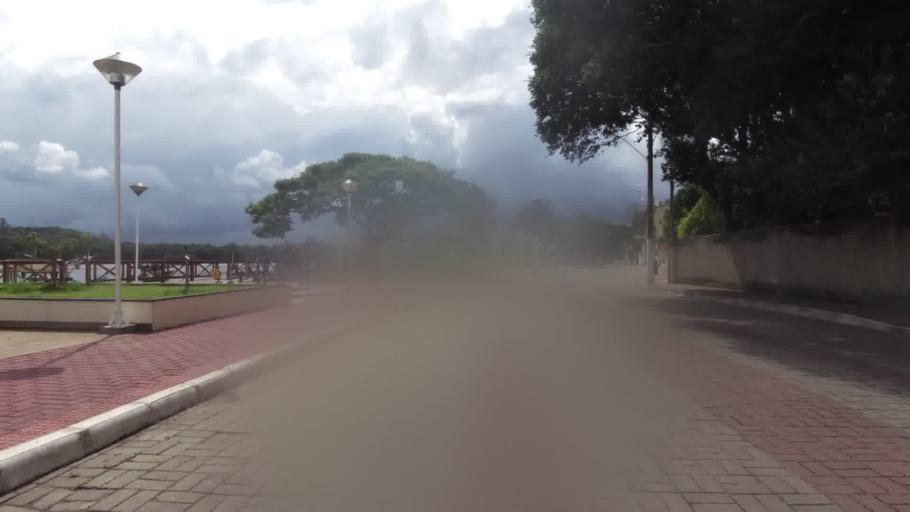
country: BR
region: Espirito Santo
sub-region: Piuma
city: Piuma
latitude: -20.8040
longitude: -40.6557
